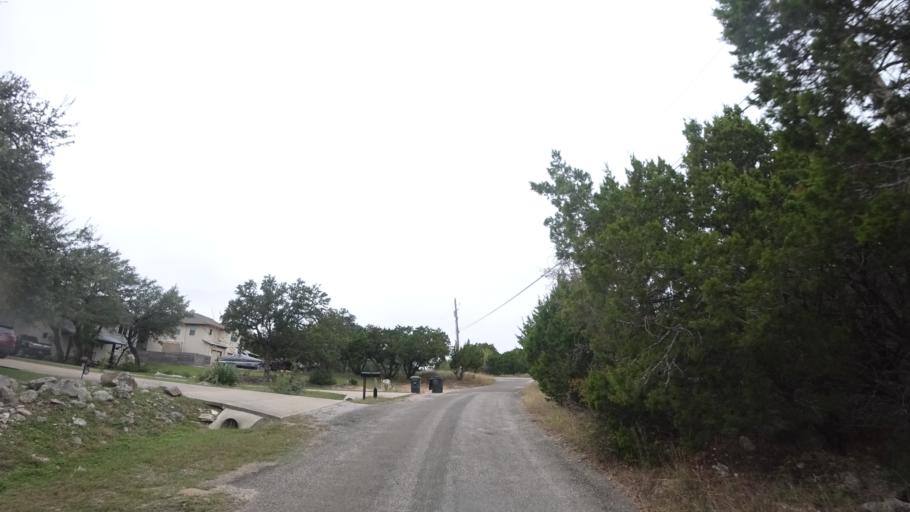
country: US
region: Texas
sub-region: Travis County
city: Hudson Bend
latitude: 30.3686
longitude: -97.9247
